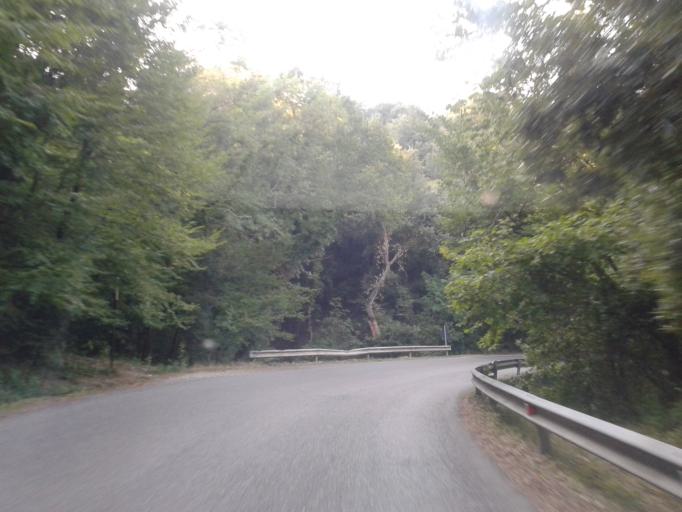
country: IT
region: Tuscany
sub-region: Provincia di Livorno
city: Rosignano Marittimo
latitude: 43.4022
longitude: 10.4889
